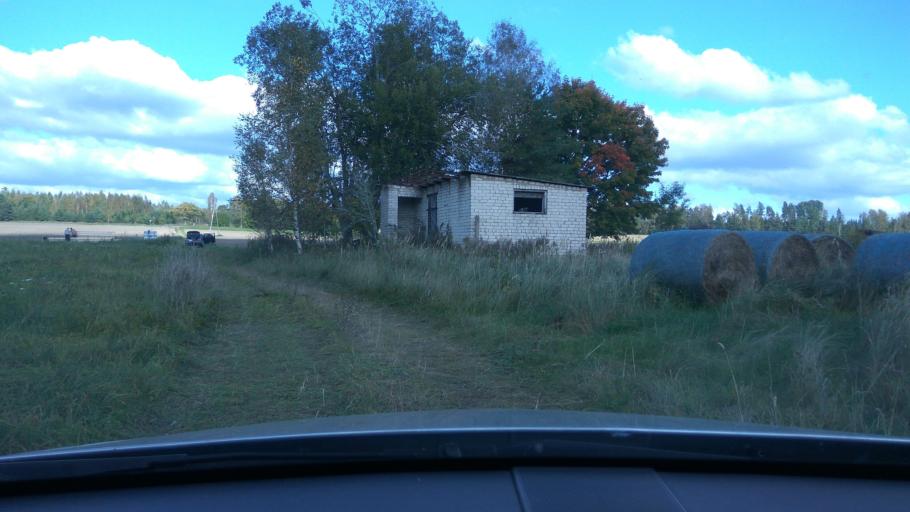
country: LV
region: Kuldigas Rajons
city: Kuldiga
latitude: 57.0236
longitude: 21.8552
